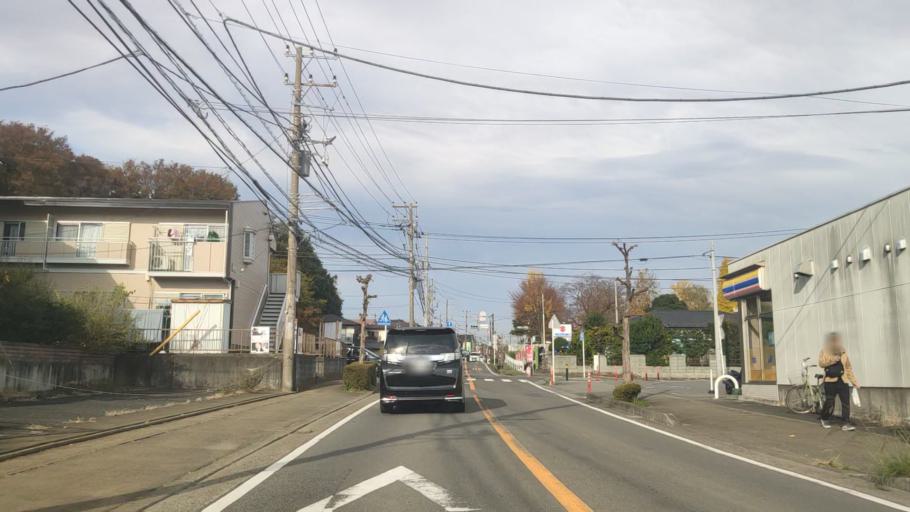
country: JP
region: Kanagawa
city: Atsugi
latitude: 35.4323
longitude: 139.4046
